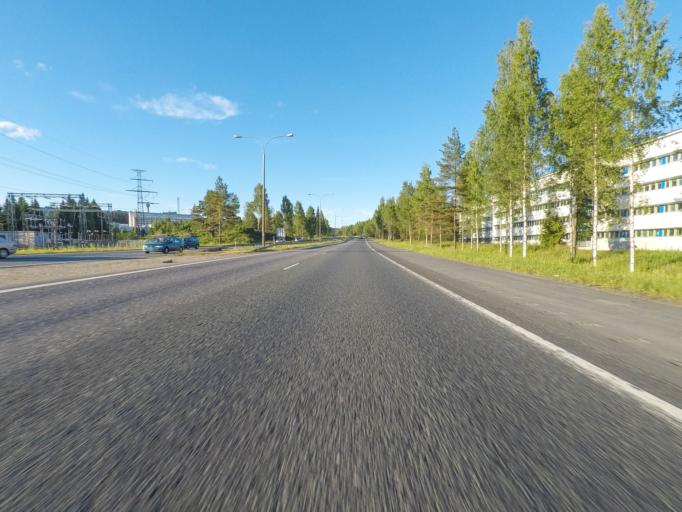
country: FI
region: Northern Savo
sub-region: Kuopio
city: Kuopio
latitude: 62.8907
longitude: 27.6392
